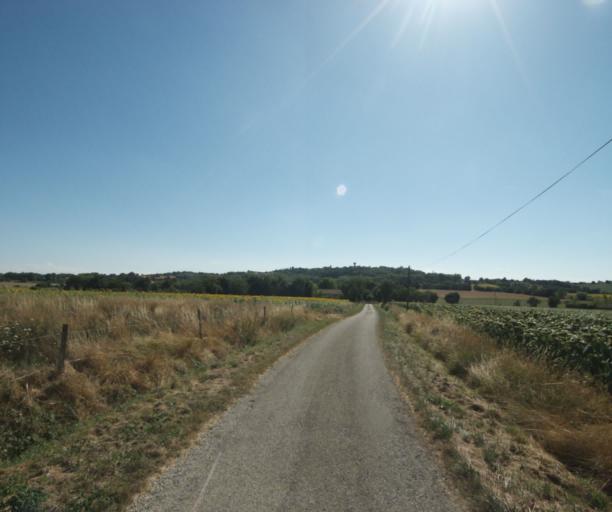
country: FR
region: Midi-Pyrenees
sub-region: Departement de la Haute-Garonne
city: Saint-Felix-Lauragais
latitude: 43.4986
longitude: 1.9110
